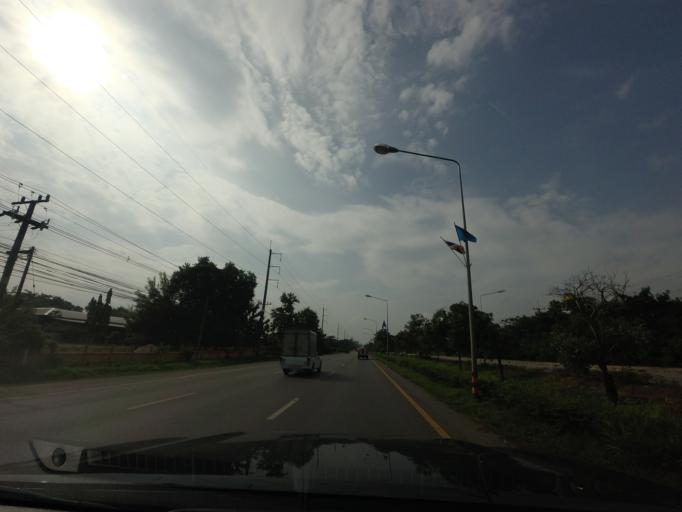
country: TH
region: Nong Khai
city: Nong Khai
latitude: 17.8286
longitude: 102.7558
